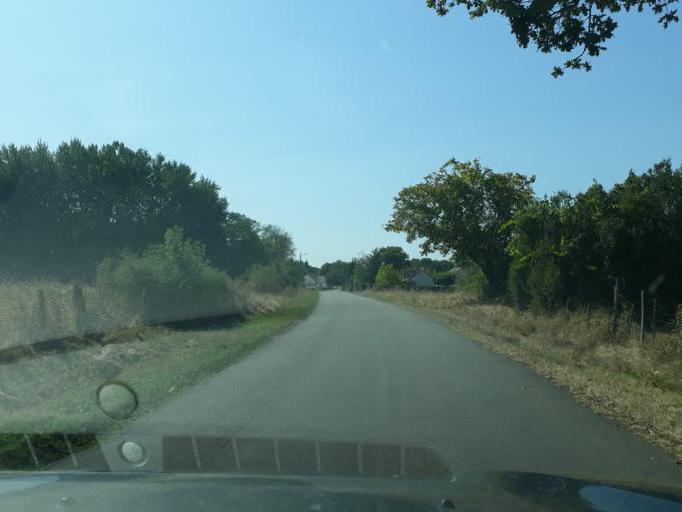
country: FR
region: Centre
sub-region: Departement du Loir-et-Cher
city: Gievres
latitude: 47.2575
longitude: 1.6798
